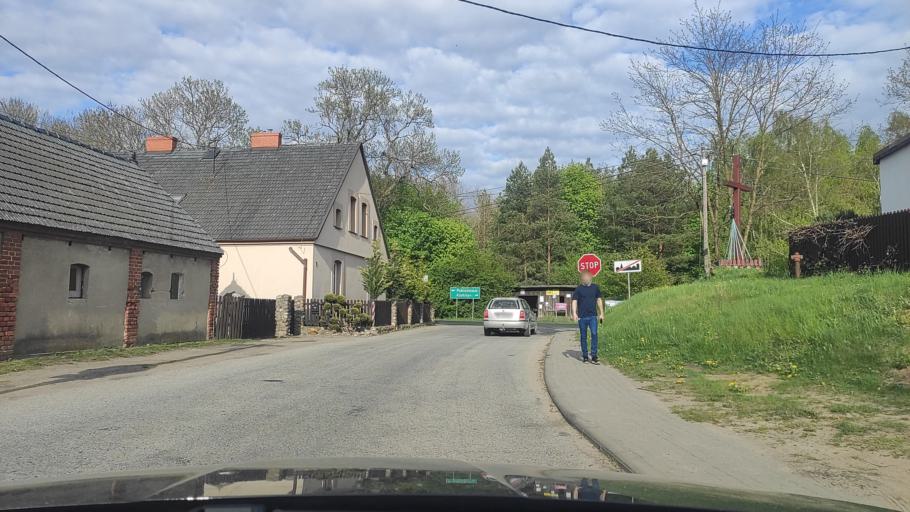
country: PL
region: Greater Poland Voivodeship
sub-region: Powiat poznanski
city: Pobiedziska
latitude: 52.4511
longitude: 17.2473
